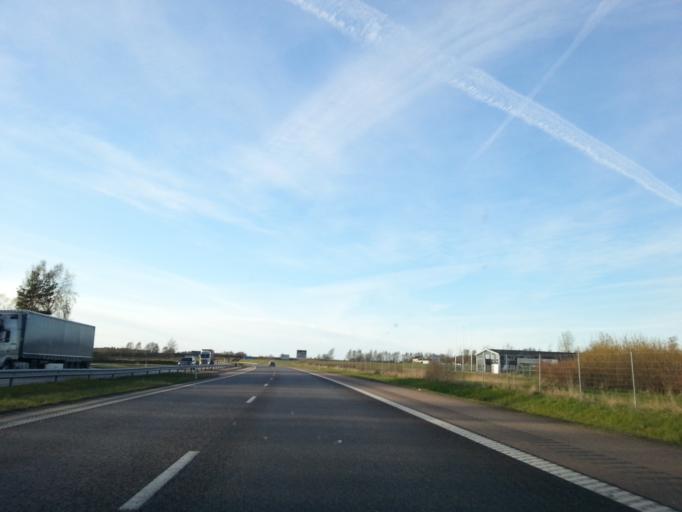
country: SE
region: Halland
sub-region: Laholms Kommun
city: Mellbystrand
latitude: 56.4440
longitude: 12.9543
